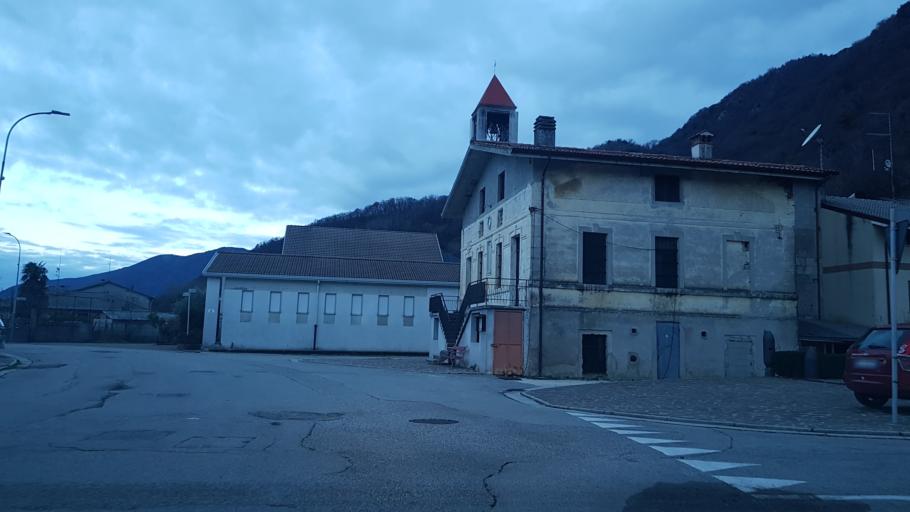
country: IT
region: Friuli Venezia Giulia
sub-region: Provincia di Udine
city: Trasaghis
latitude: 46.2869
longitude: 13.0929
